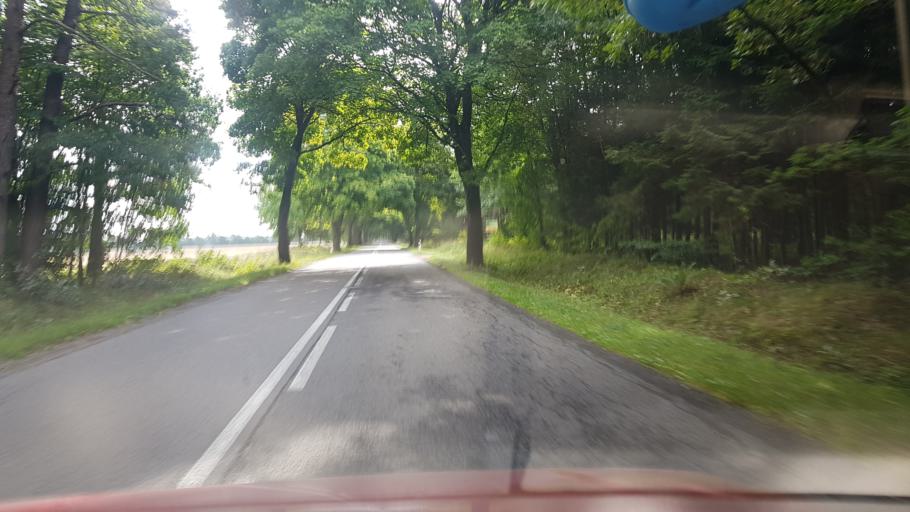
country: PL
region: West Pomeranian Voivodeship
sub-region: Powiat koszalinski
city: Polanow
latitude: 54.1136
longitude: 16.7772
